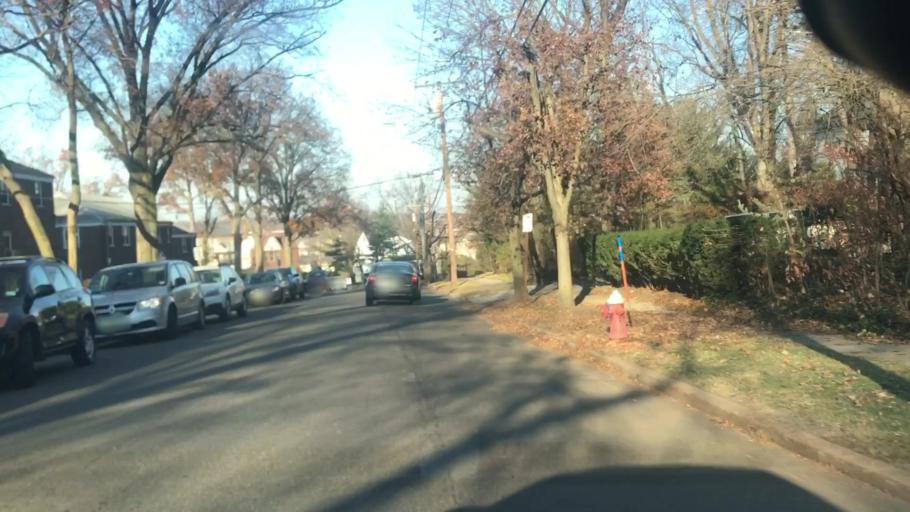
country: US
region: New Jersey
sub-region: Bergen County
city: Englewood
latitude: 40.8843
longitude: -73.9765
